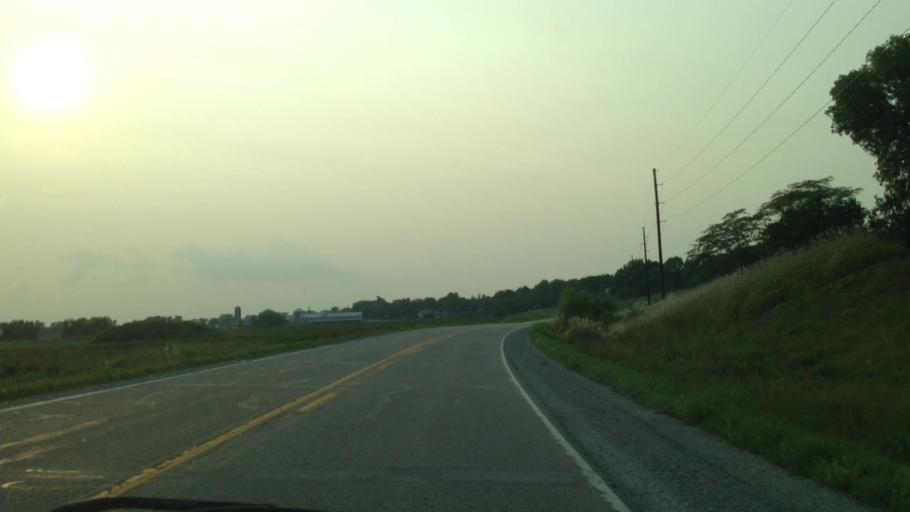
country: US
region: Iowa
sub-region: Benton County
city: Walford
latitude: 41.7989
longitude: -91.9302
